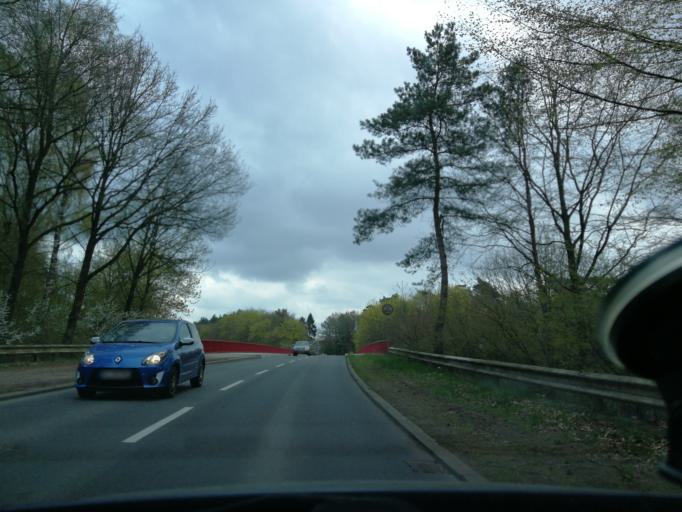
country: DE
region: Hamburg
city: Harburg
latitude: 53.4482
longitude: 9.9185
